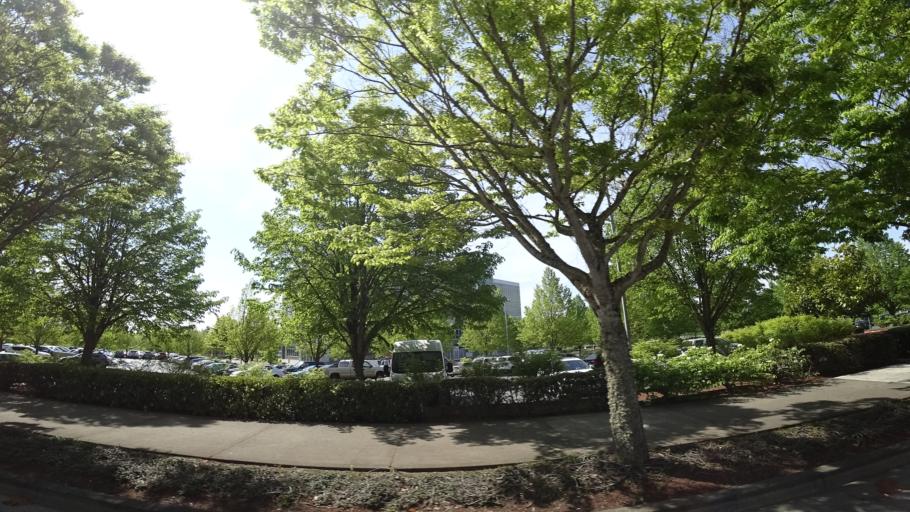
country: US
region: Oregon
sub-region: Washington County
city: Rockcreek
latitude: 45.5346
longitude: -122.9036
